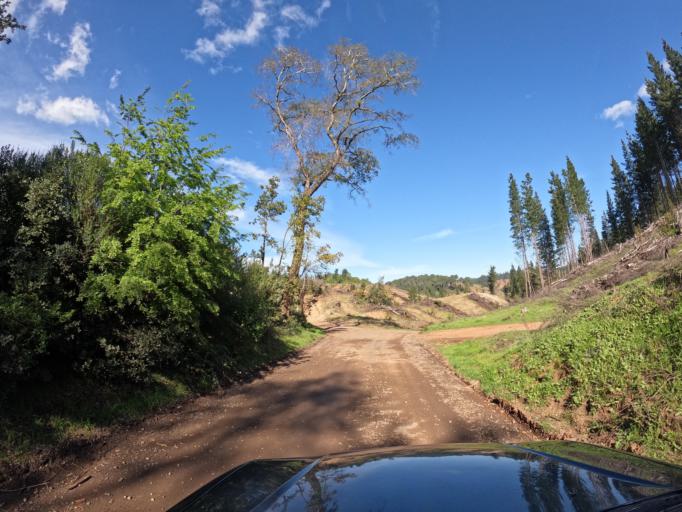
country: CL
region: Biobio
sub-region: Provincia de Concepcion
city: Chiguayante
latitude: -37.0740
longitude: -72.8379
